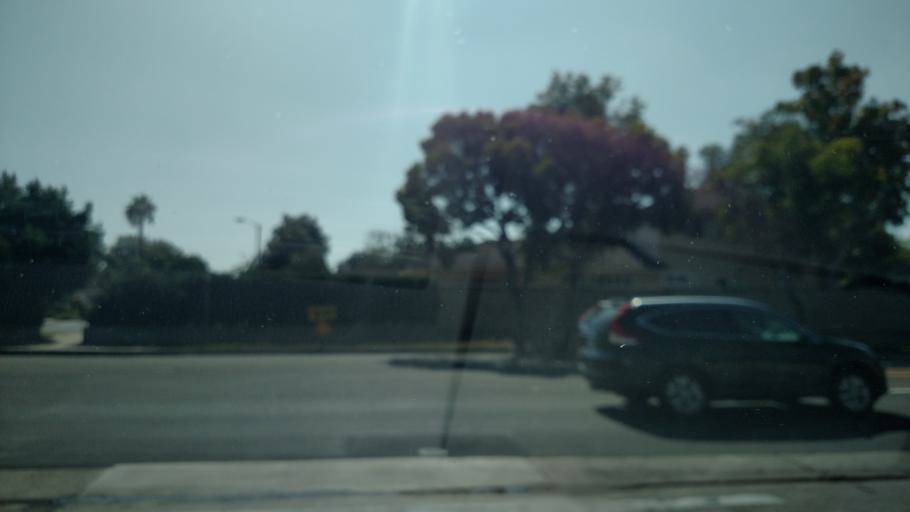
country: US
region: California
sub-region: Orange County
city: Irvine
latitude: 33.6638
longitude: -117.8228
